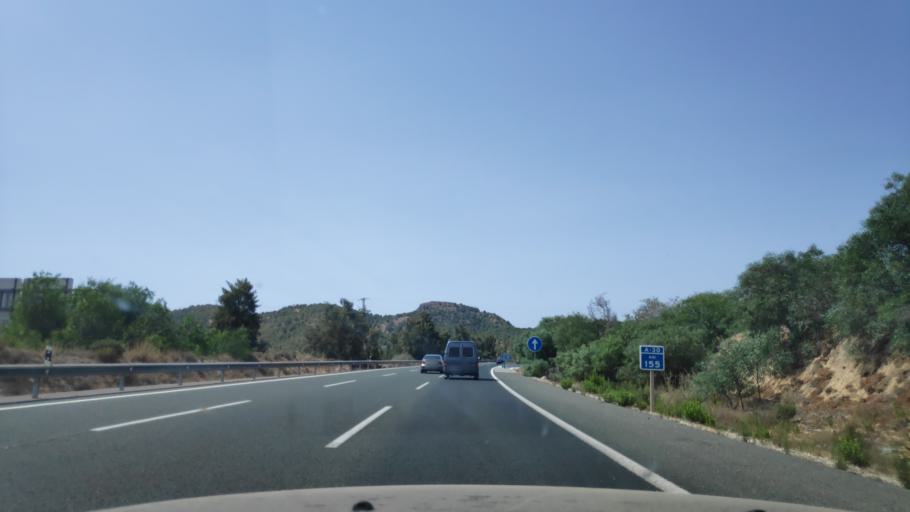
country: ES
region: Murcia
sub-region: Murcia
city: Murcia
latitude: 37.8863
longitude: -1.1388
